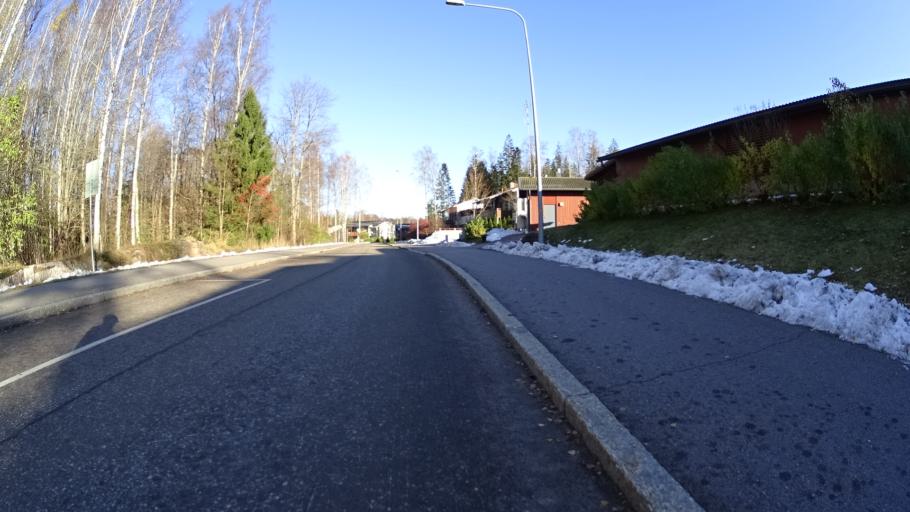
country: FI
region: Uusimaa
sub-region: Helsinki
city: Kauniainen
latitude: 60.2059
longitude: 24.7153
